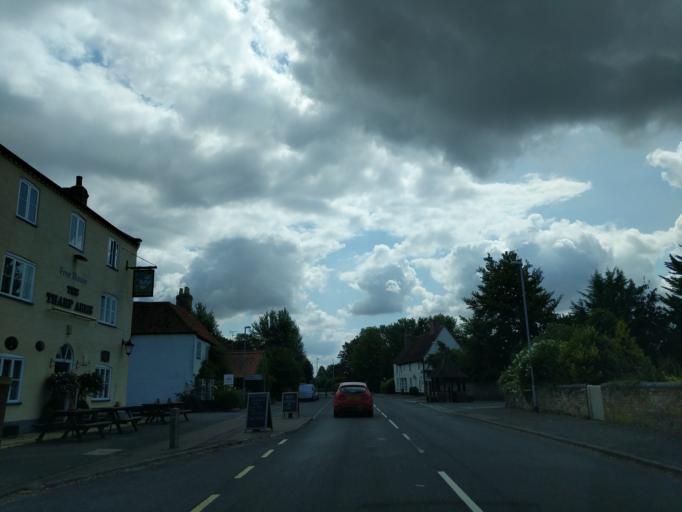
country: GB
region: England
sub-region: Cambridgeshire
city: Isleham
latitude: 52.3023
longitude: 0.4359
